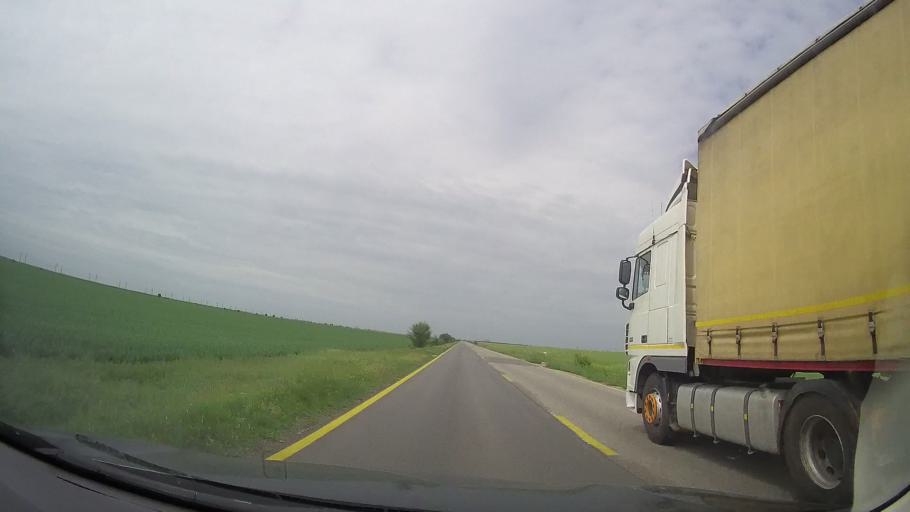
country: RO
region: Olt
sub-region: Comuna Mihaesti
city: Mihaesti
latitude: 44.1207
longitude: 24.7607
